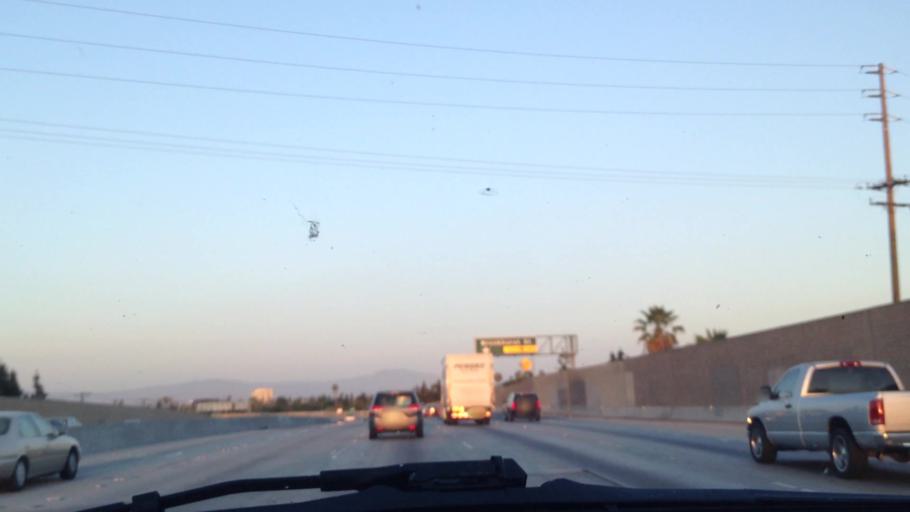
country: US
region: California
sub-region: Orange County
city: Buena Park
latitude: 33.8544
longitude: -117.9679
